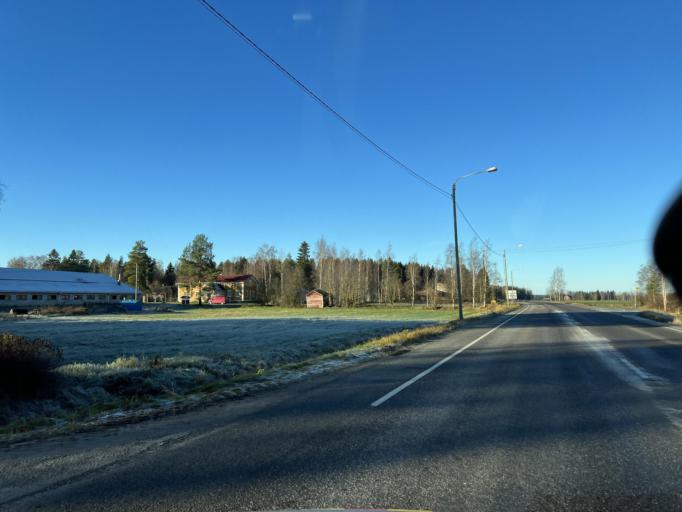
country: FI
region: Northern Ostrobothnia
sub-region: Nivala-Haapajaervi
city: Nivala
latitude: 63.9556
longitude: 24.8623
